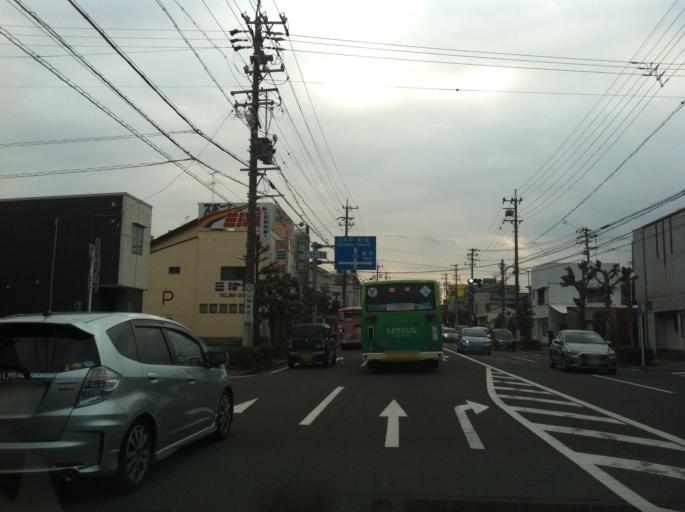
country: JP
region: Shizuoka
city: Shizuoka-shi
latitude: 35.0104
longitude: 138.4855
